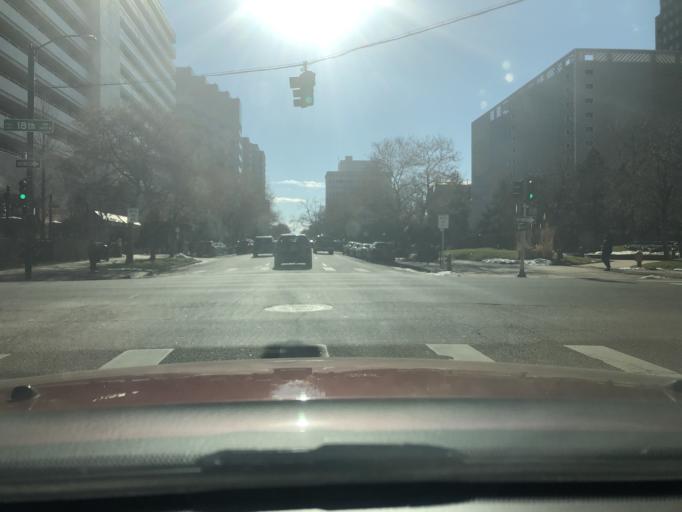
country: US
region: Colorado
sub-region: Denver County
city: Denver
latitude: 39.7450
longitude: -104.9836
